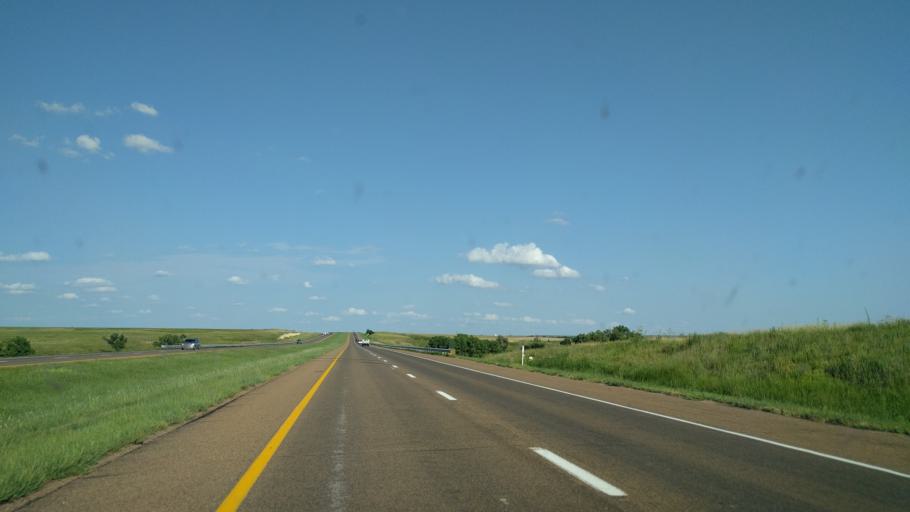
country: US
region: Kansas
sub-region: Ellis County
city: Ellis
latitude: 38.9418
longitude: -99.4962
